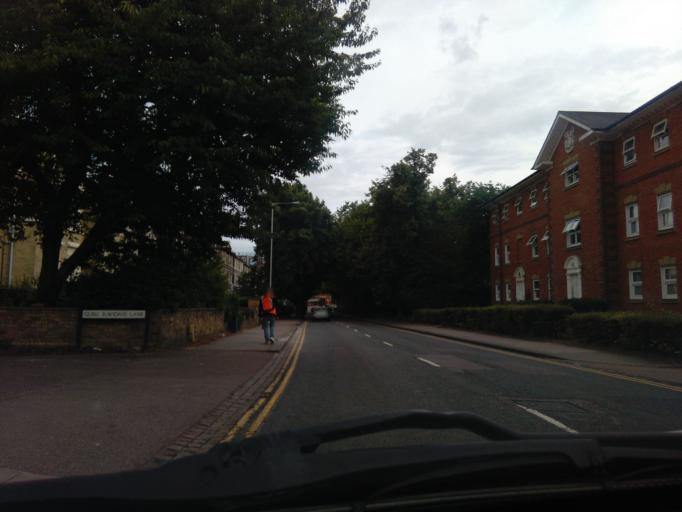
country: GB
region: England
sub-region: Bedford
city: Bedford
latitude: 52.1381
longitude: -0.4795
